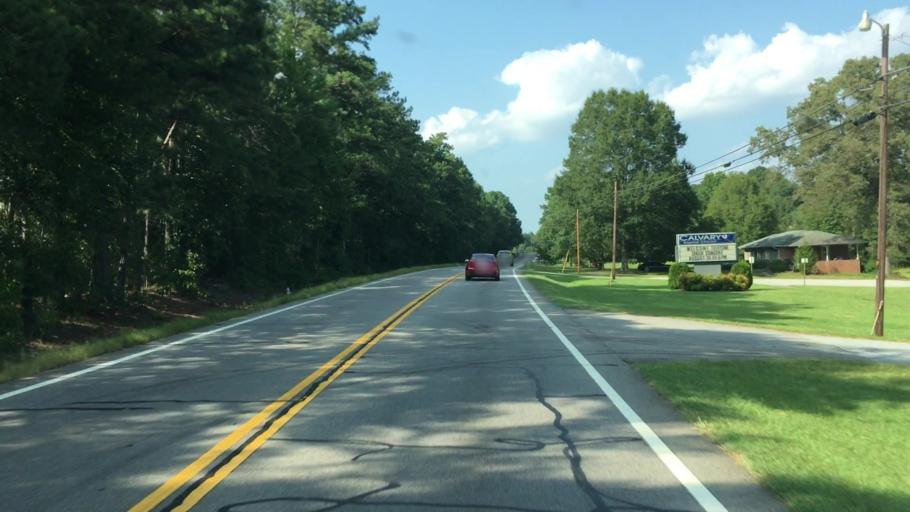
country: US
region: Georgia
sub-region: Walton County
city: Monroe
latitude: 33.7530
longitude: -83.7015
